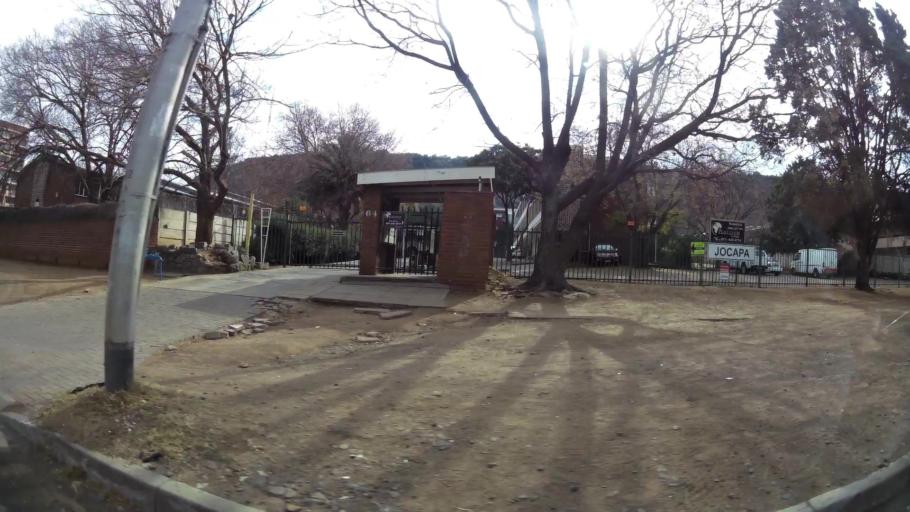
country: ZA
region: Orange Free State
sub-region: Mangaung Metropolitan Municipality
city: Bloemfontein
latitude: -29.1048
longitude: 26.2377
